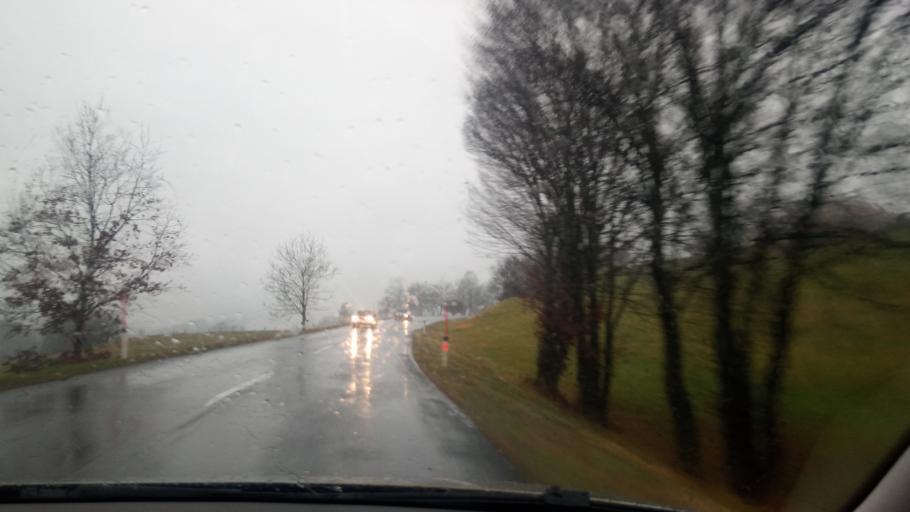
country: AT
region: Carinthia
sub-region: Politischer Bezirk Klagenfurt Land
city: Keutschach am See
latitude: 46.5891
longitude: 14.1766
